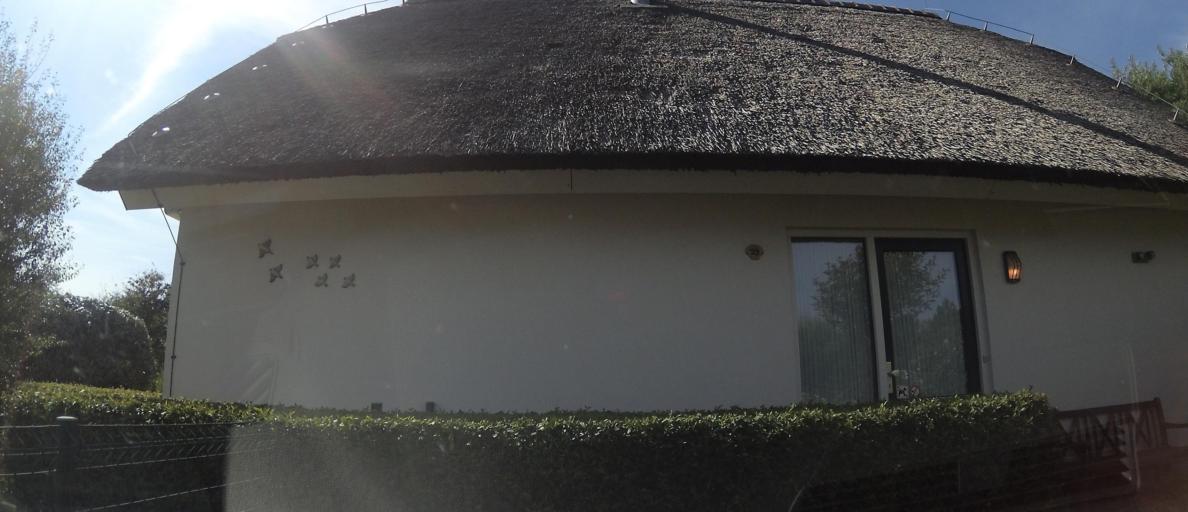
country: NL
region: North Holland
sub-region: Gemeente Den Helder
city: Den Helder
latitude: 52.9074
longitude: 4.7233
